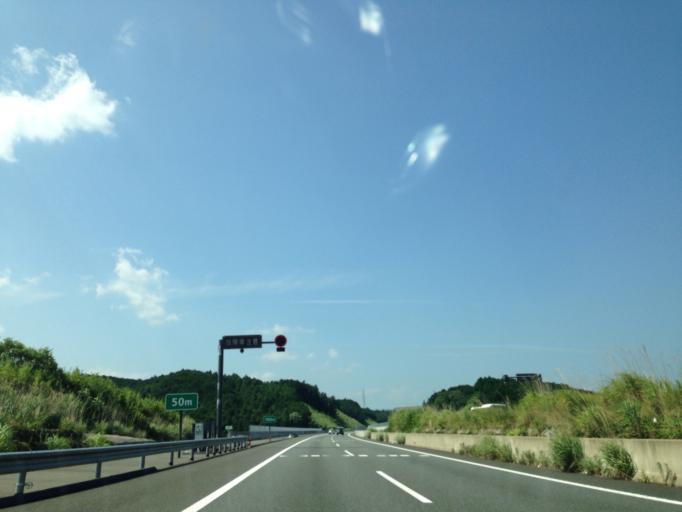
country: JP
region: Shizuoka
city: Mishima
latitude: 35.2110
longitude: 138.8861
